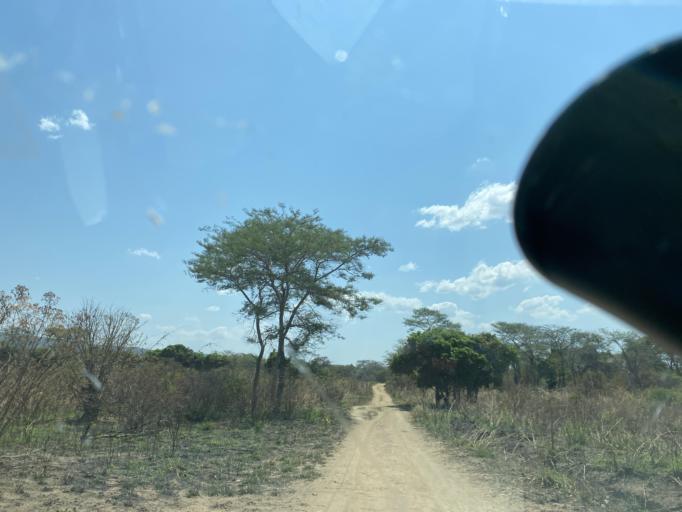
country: ZM
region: Lusaka
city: Chongwe
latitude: -15.0817
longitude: 29.5072
